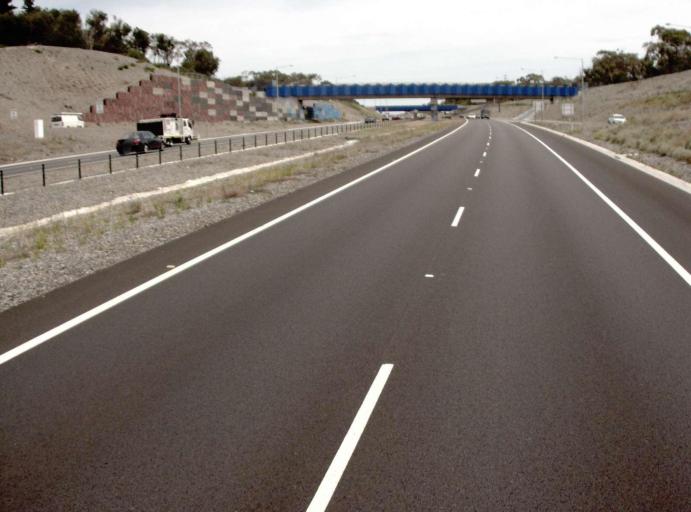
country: AU
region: Victoria
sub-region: Frankston
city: Langwarrin
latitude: -38.1572
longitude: 145.1675
